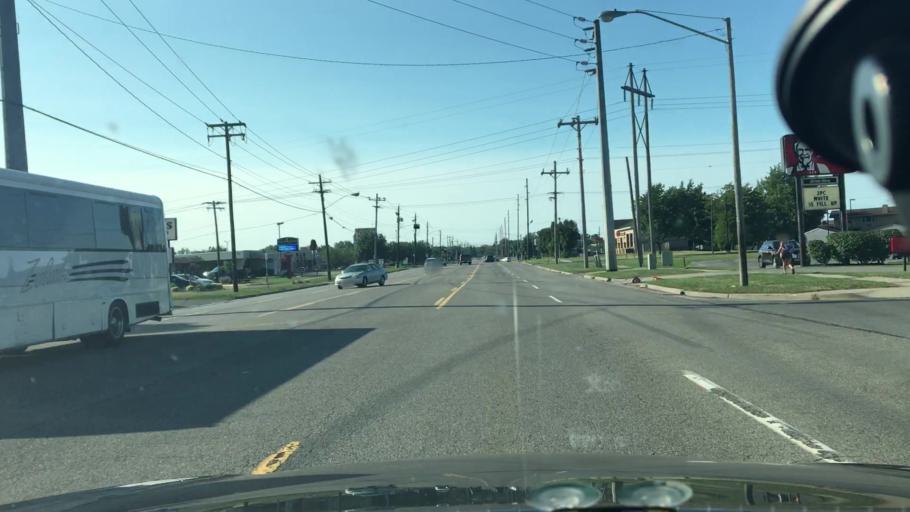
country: US
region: New York
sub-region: Erie County
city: Cheektowaga
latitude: 42.9163
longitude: -78.7357
